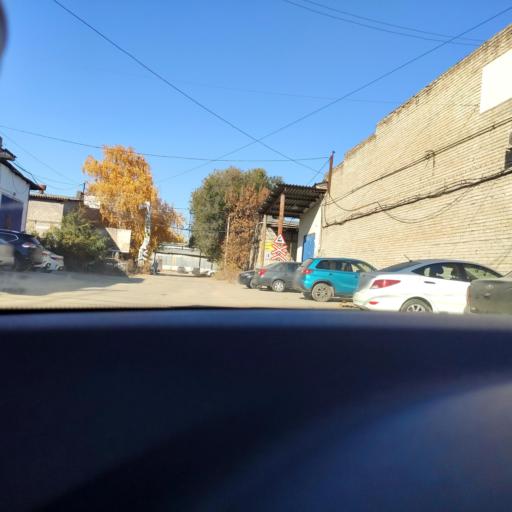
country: RU
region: Samara
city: Petra-Dubrava
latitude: 53.2459
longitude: 50.3003
